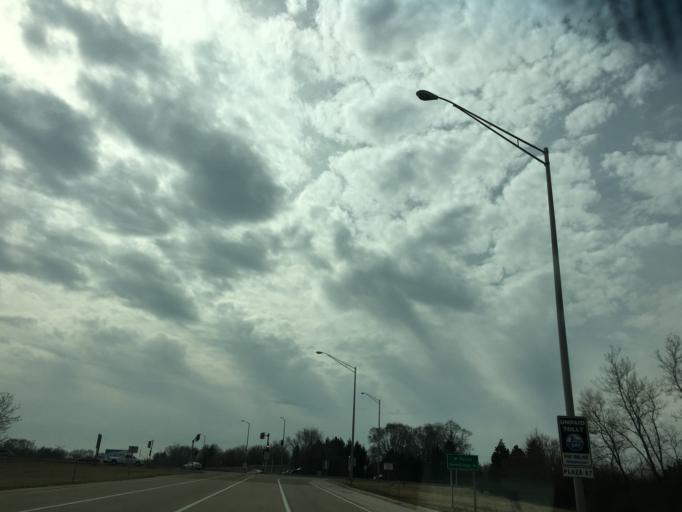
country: US
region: Illinois
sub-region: DuPage County
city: Woodridge
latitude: 41.7517
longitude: -88.0361
